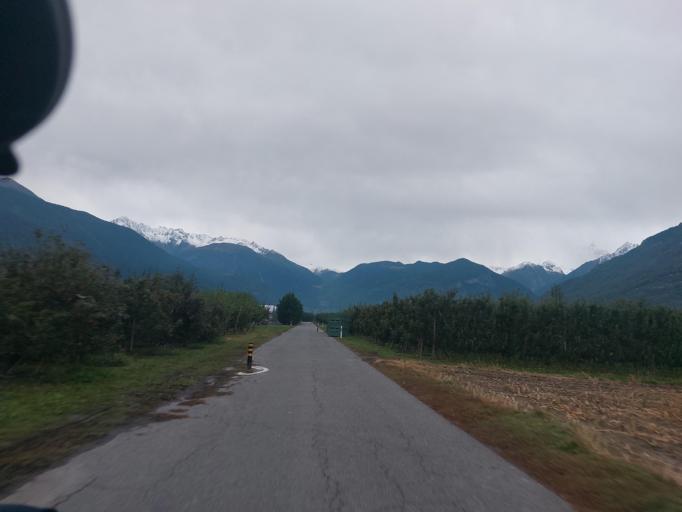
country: CH
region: Valais
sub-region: Martigny District
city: Charrat-les-Chenes
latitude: 46.1406
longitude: 7.1386
